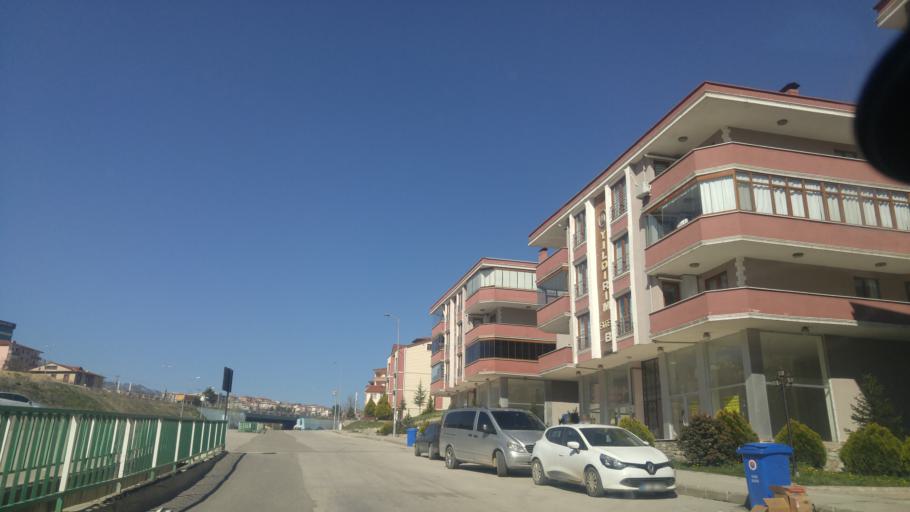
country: TR
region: Karabuk
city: Karabuk
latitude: 41.2226
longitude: 32.6626
